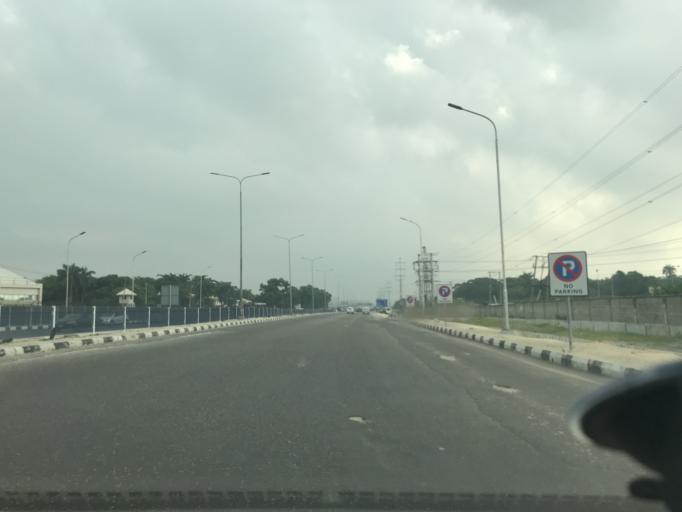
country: NG
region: Lagos
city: Ikoyi
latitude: 6.4413
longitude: 3.5314
